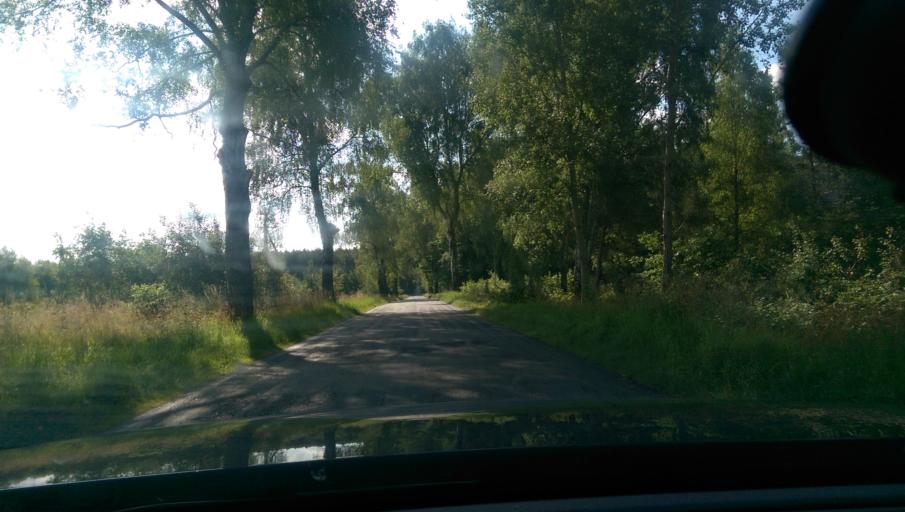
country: PL
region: West Pomeranian Voivodeship
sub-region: Powiat walecki
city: Walcz
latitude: 53.3659
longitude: 16.5129
